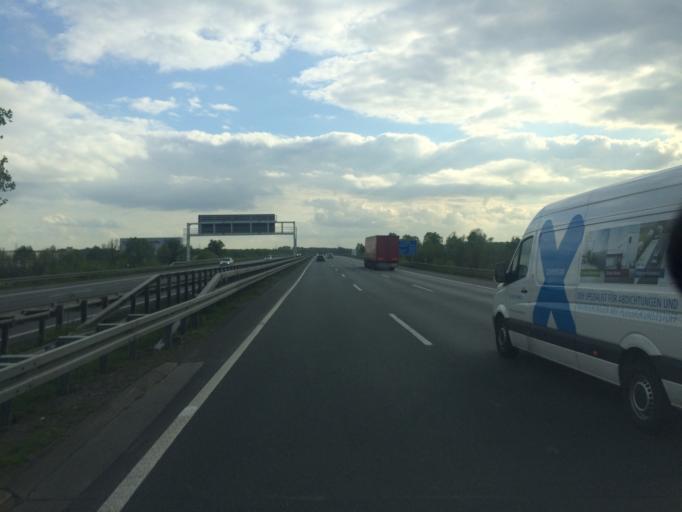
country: DE
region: North Rhine-Westphalia
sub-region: Regierungsbezirk Arnsberg
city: Welver
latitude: 51.6914
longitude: 7.9653
